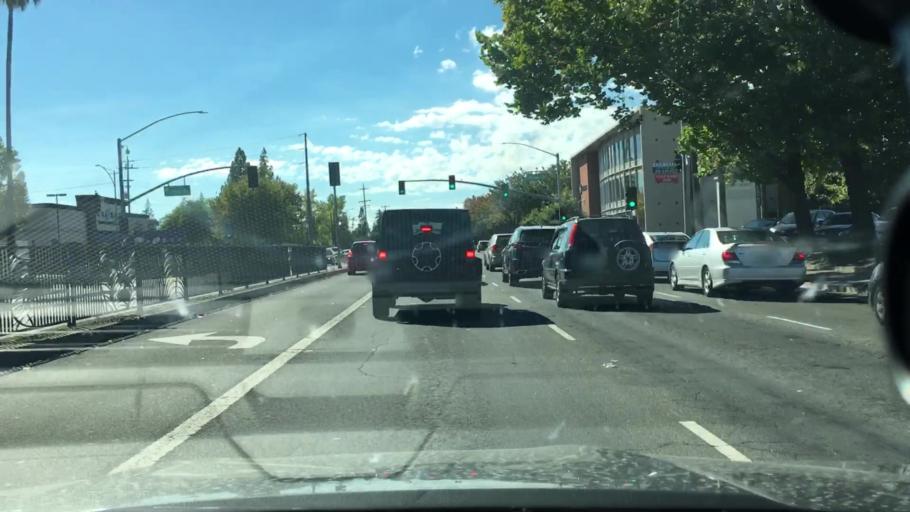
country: US
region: California
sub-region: Sacramento County
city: Arden-Arcade
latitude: 38.6073
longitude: -121.3830
